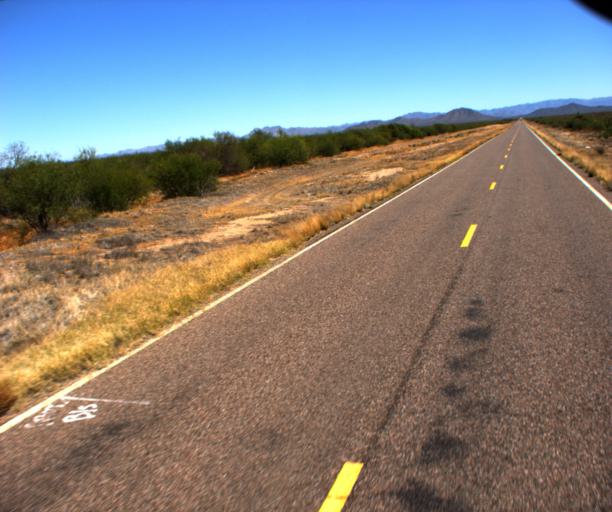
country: US
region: Arizona
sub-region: Yavapai County
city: Congress
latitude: 34.0352
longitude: -113.0776
